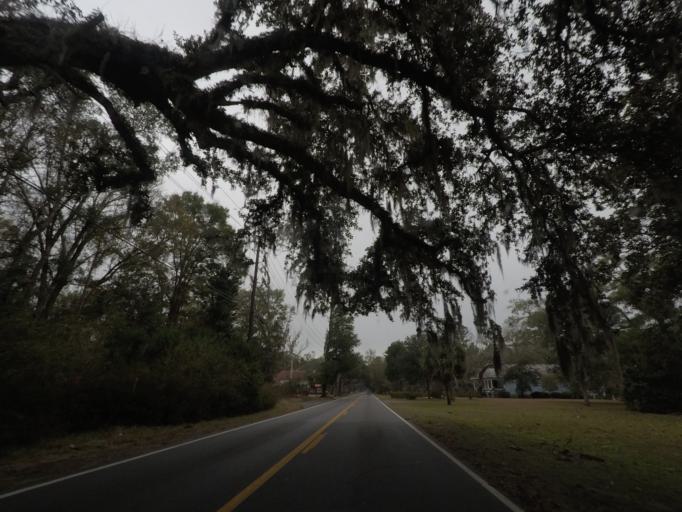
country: US
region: South Carolina
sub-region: Charleston County
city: Hollywood
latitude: 32.7181
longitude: -80.3489
